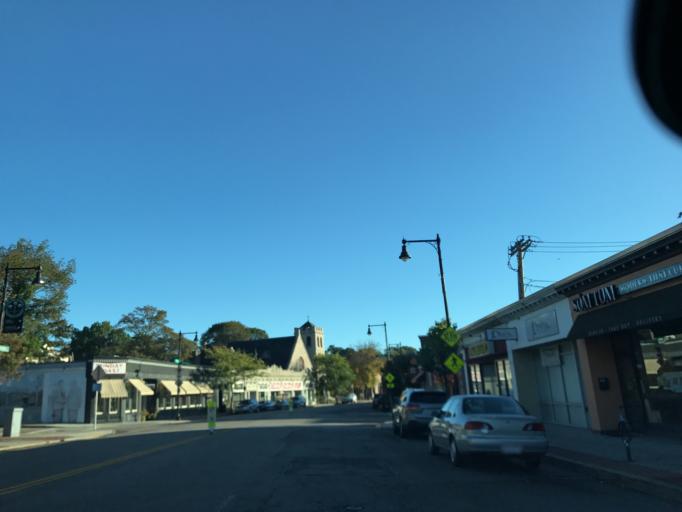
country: US
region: Massachusetts
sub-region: Suffolk County
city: Jamaica Plain
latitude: 42.2853
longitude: -71.1562
